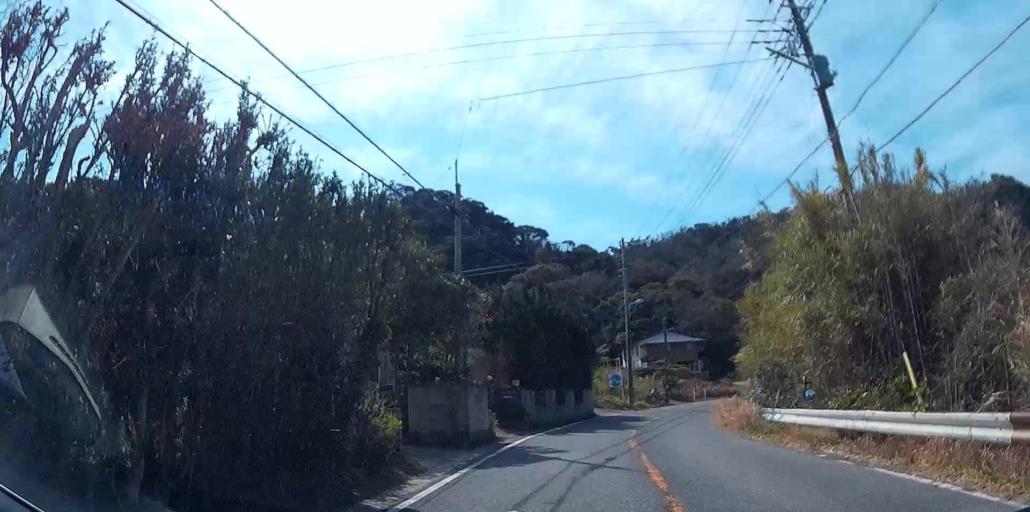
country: JP
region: Chiba
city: Tateyama
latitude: 34.9742
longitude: 139.7696
